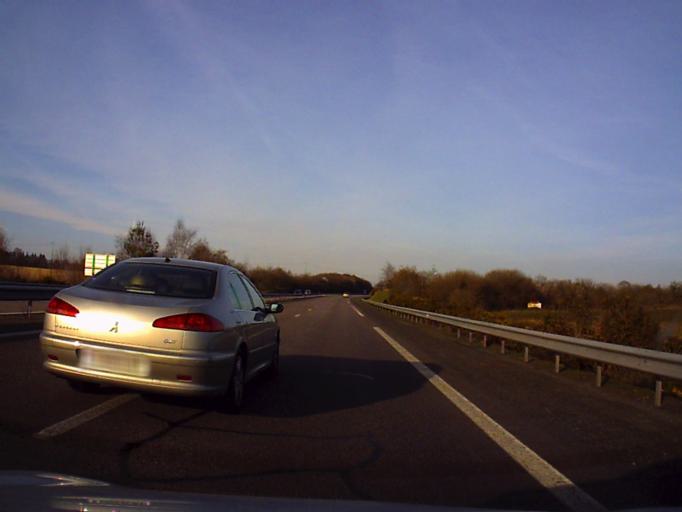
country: FR
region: Brittany
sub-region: Departement d'Ille-et-Vilaine
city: Plelan-le-Grand
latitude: 48.0141
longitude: -2.0669
